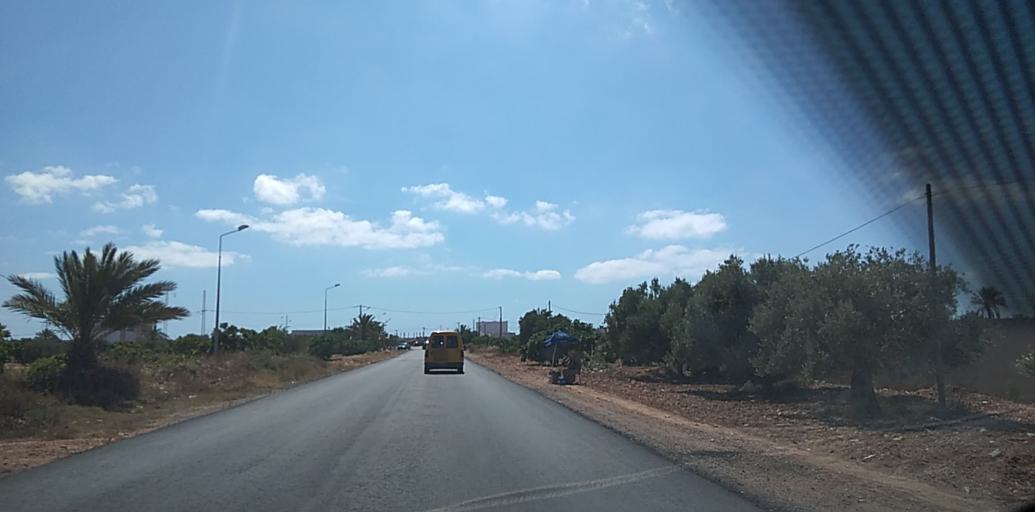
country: TN
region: Safaqis
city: Al Qarmadah
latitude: 34.6566
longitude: 11.0883
